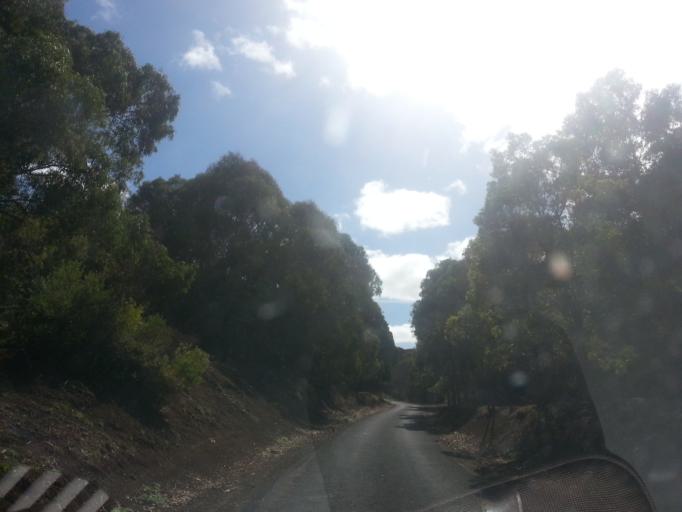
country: AU
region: Victoria
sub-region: Warrnambool
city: Warrnambool
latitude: -38.3256
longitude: 142.3654
